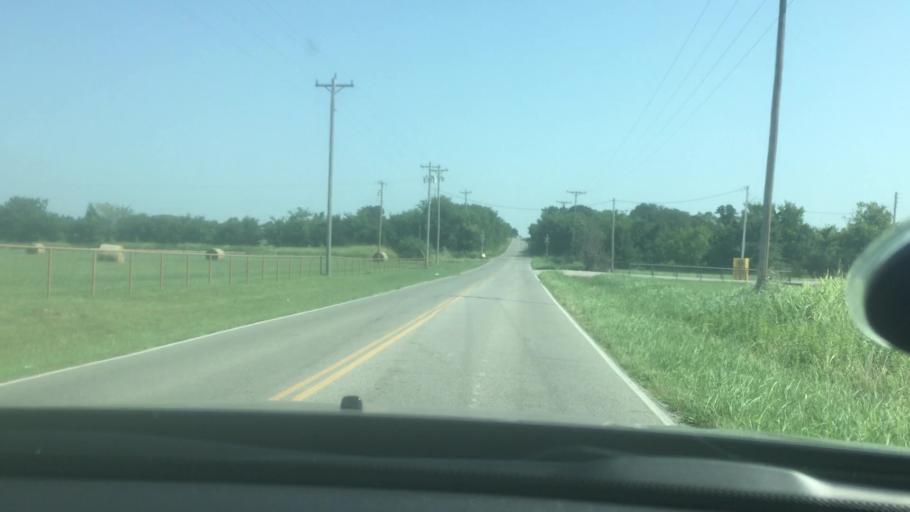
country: US
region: Oklahoma
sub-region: Bryan County
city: Calera
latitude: 34.0074
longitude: -96.4656
